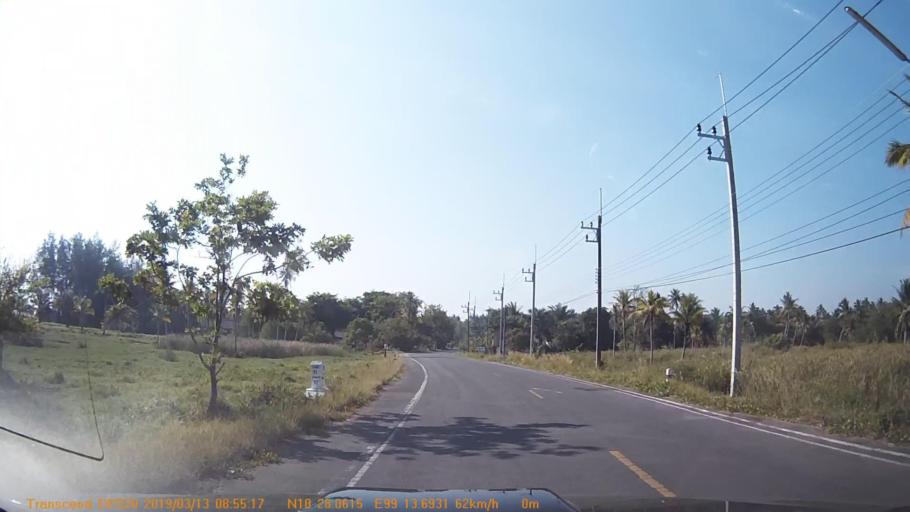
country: TH
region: Chumphon
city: Chumphon
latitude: 10.4674
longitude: 99.2283
